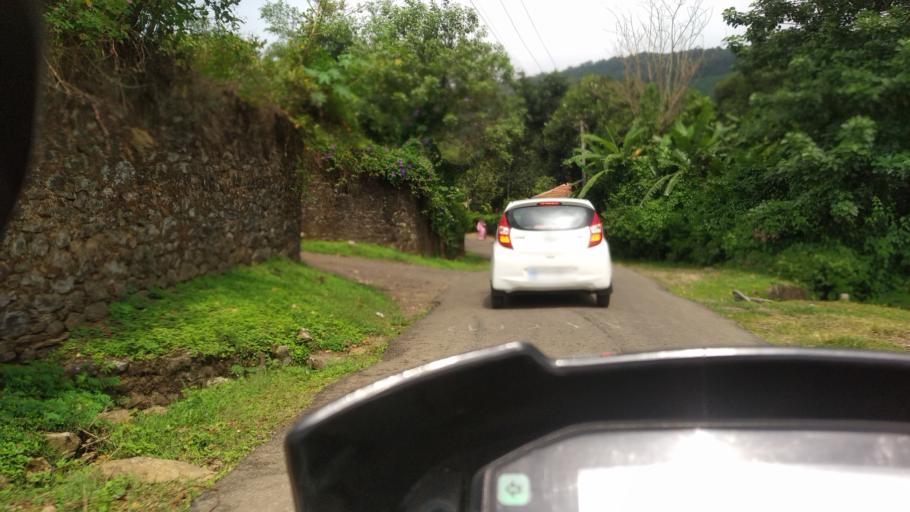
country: IN
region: Tamil Nadu
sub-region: Theni
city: Gudalur
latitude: 9.5788
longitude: 77.0145
